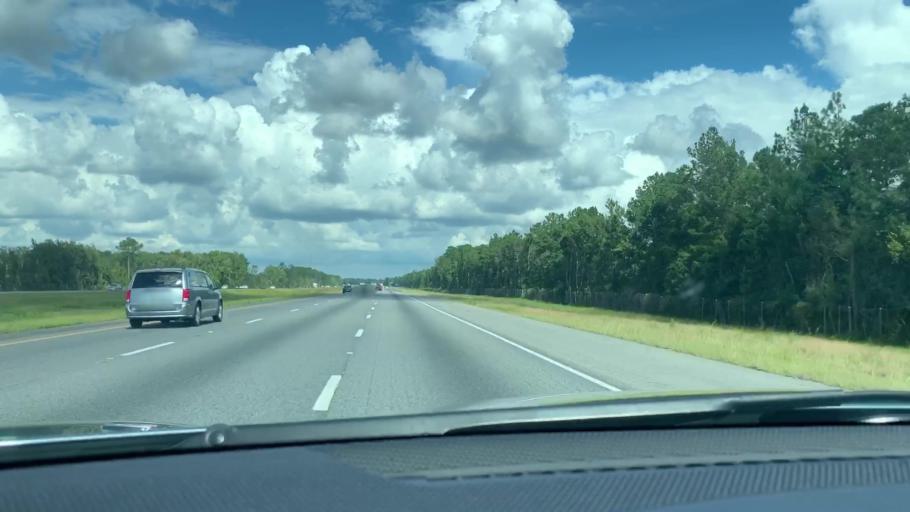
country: US
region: Georgia
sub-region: Glynn County
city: Brunswick
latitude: 31.0752
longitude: -81.6199
